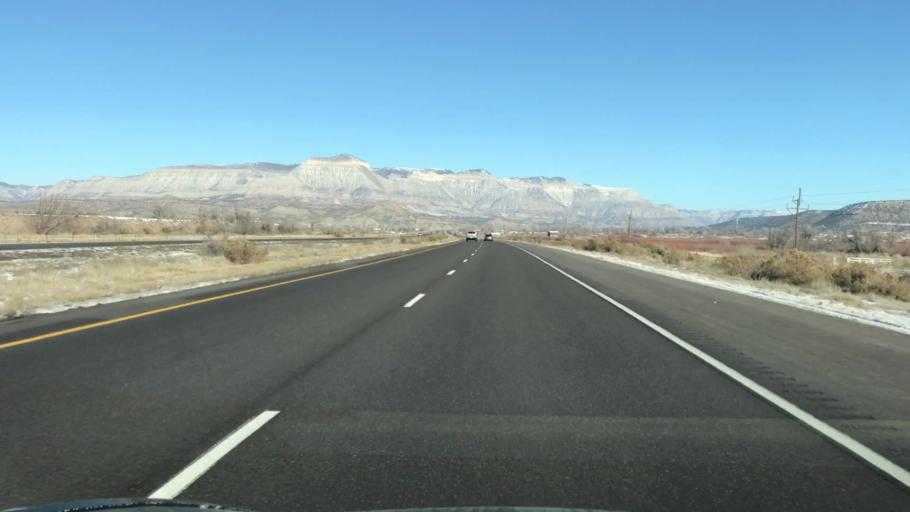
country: US
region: Colorado
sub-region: Mesa County
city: Palisade
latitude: 39.2921
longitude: -108.2234
